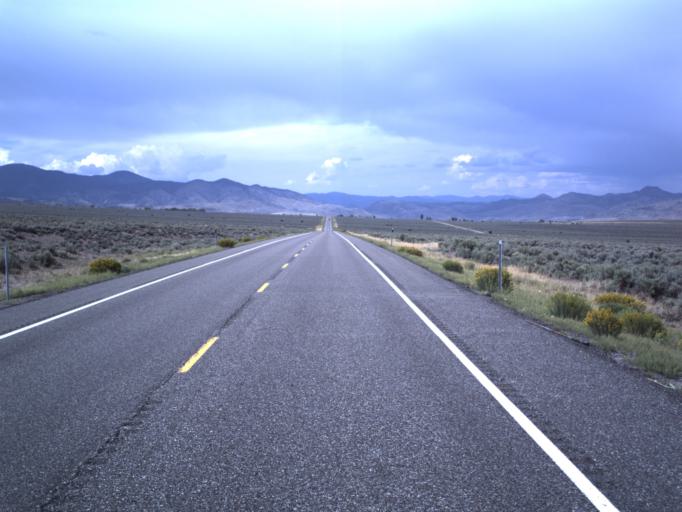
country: US
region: Utah
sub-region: Piute County
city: Junction
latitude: 38.3587
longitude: -112.2222
